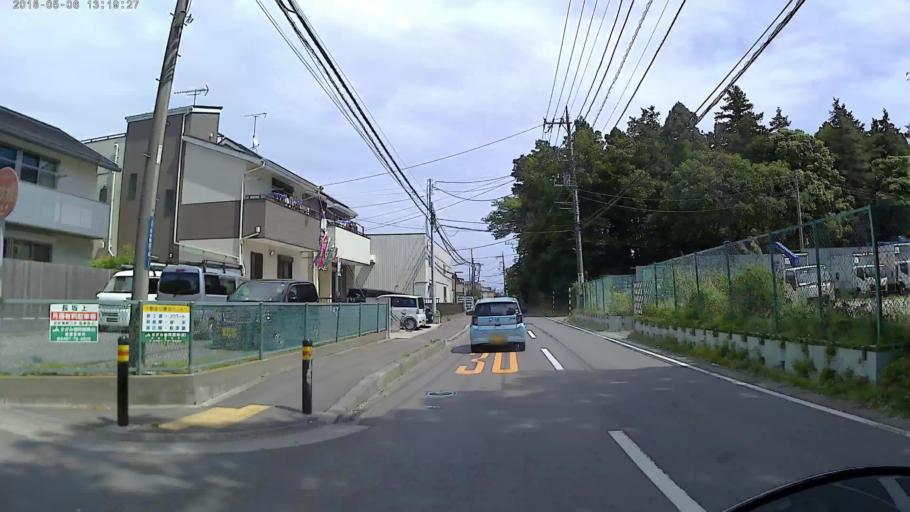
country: JP
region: Kanagawa
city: Minami-rinkan
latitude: 35.4142
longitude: 139.4405
